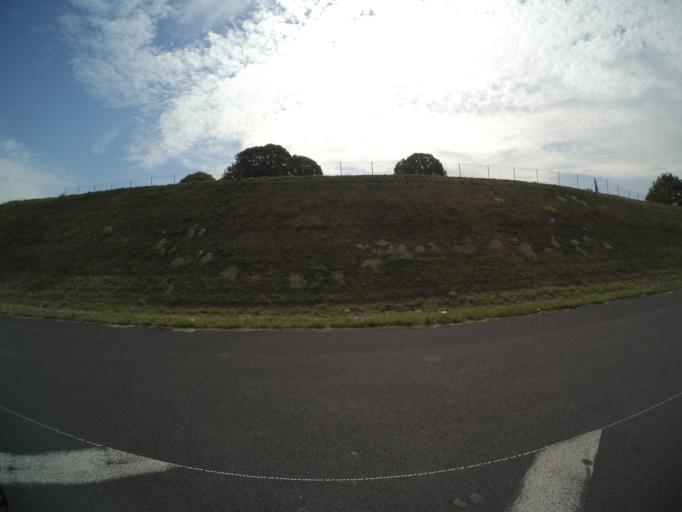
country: FR
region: Pays de la Loire
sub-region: Departement de Maine-et-Loire
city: Distre
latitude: 47.2137
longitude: -0.1793
